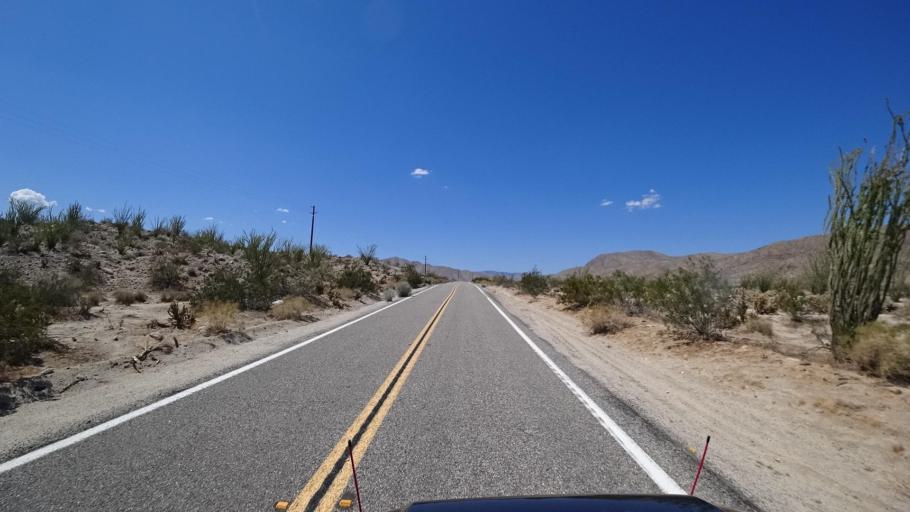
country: US
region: California
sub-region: San Diego County
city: Borrego Springs
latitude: 33.1332
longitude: -116.3169
